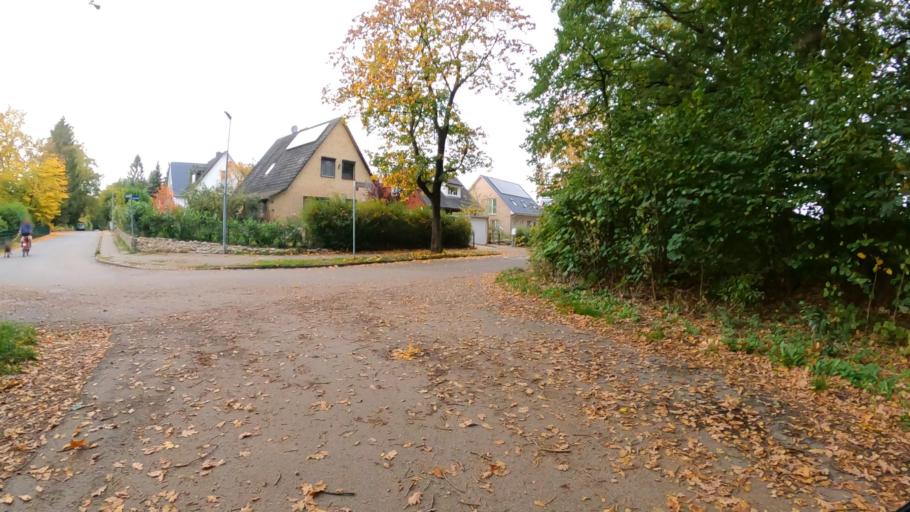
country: DE
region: Schleswig-Holstein
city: Ahrensburg
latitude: 53.6514
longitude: 10.2441
